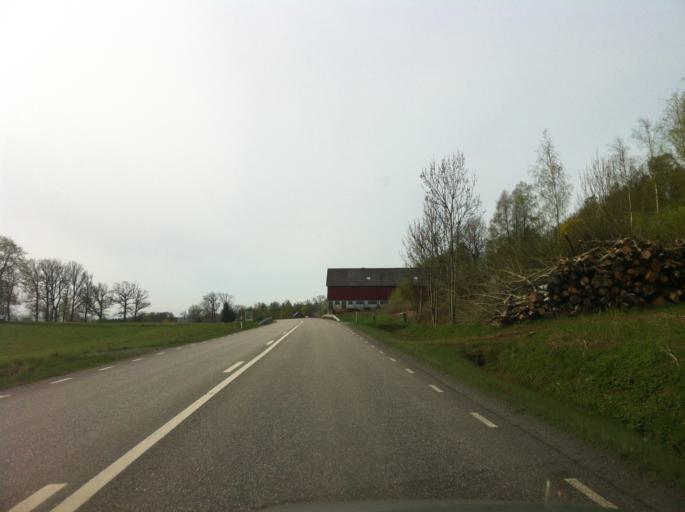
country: SE
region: Vaestra Goetaland
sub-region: Harryda Kommun
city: Ravlanda
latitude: 57.5399
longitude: 12.5318
